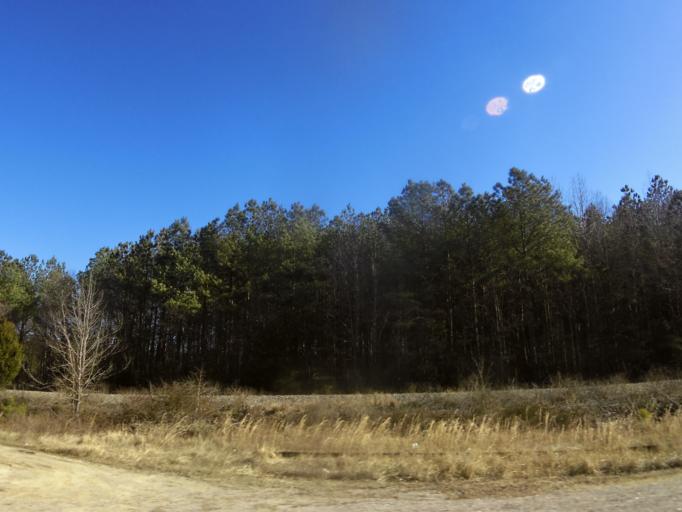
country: US
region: Virginia
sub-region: City of Petersburg
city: Petersburg
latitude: 37.1856
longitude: -77.4221
